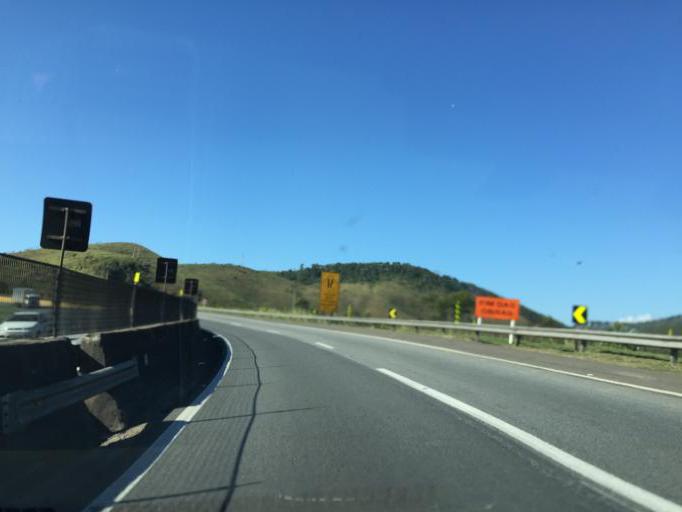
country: BR
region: Sao Paulo
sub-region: Cruzeiro
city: Cruzeiro
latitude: -22.6243
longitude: -44.9113
